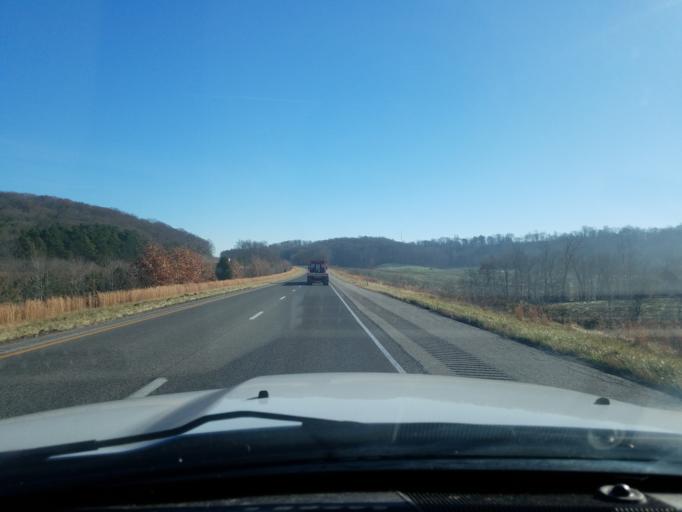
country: US
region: Indiana
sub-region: Dubois County
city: Ferdinand
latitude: 38.2117
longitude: -86.7580
